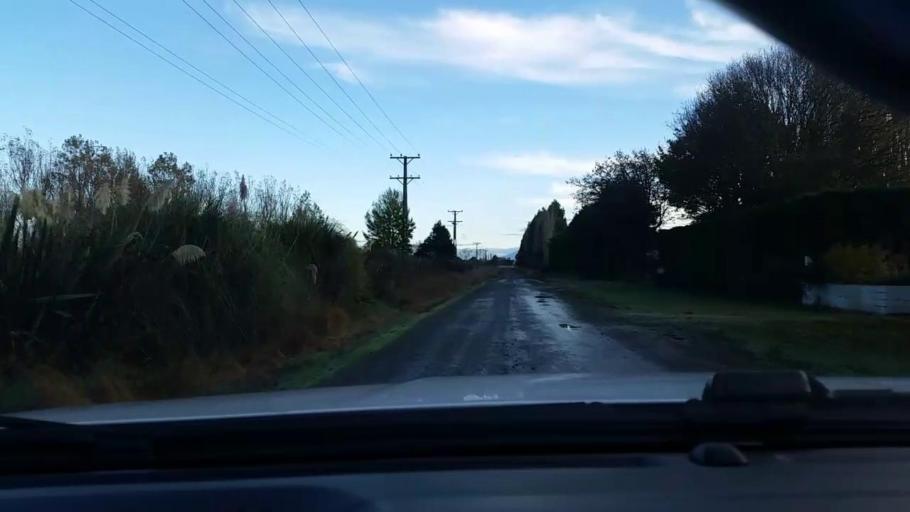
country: NZ
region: Southland
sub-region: Southland District
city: Winton
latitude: -46.1500
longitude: 168.2557
